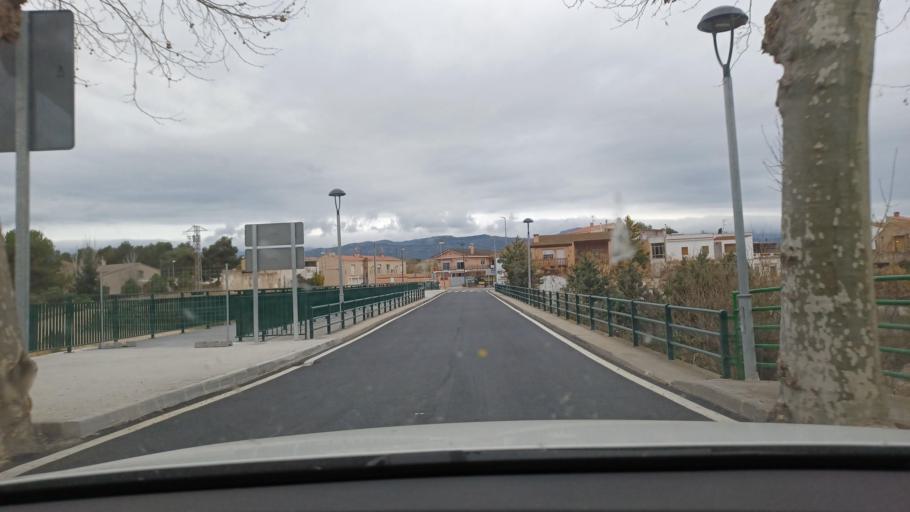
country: ES
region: Catalonia
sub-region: Provincia de Tarragona
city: Ulldecona
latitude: 40.6075
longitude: 0.3476
